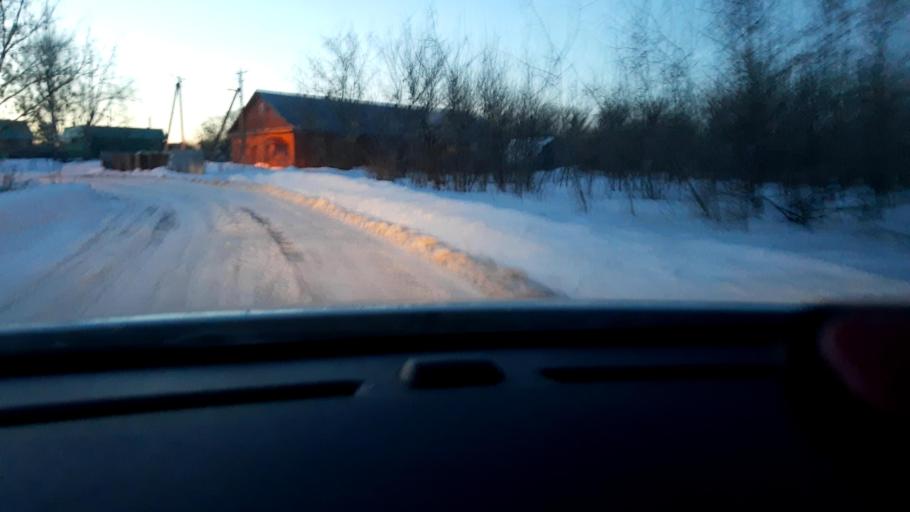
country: RU
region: Bashkortostan
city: Avdon
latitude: 54.3860
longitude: 55.6934
